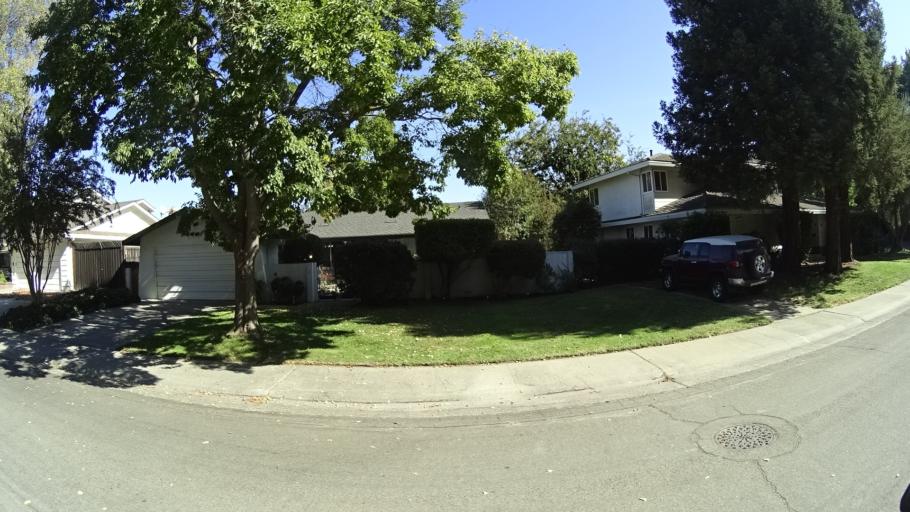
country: US
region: California
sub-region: Sacramento County
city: Parkway
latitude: 38.5052
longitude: -121.5257
